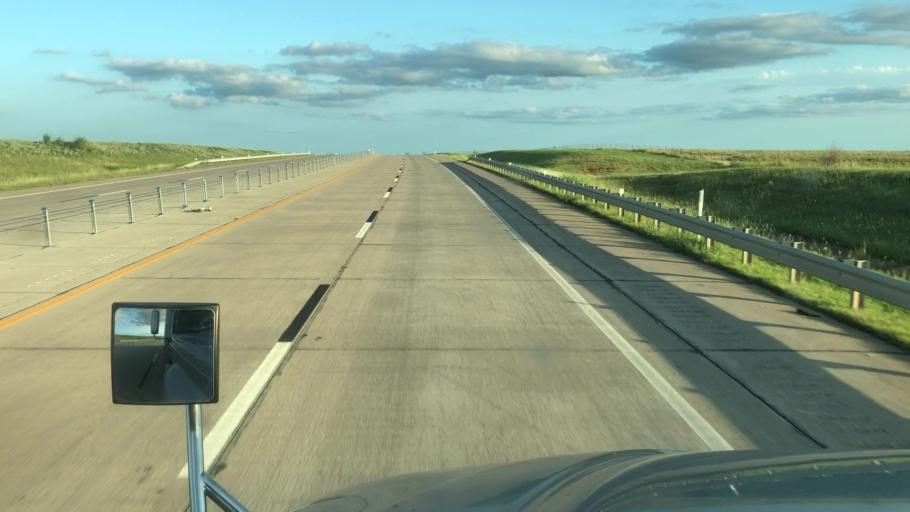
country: US
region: Oklahoma
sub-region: Pawnee County
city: Pawnee
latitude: 36.3498
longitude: -97.0292
